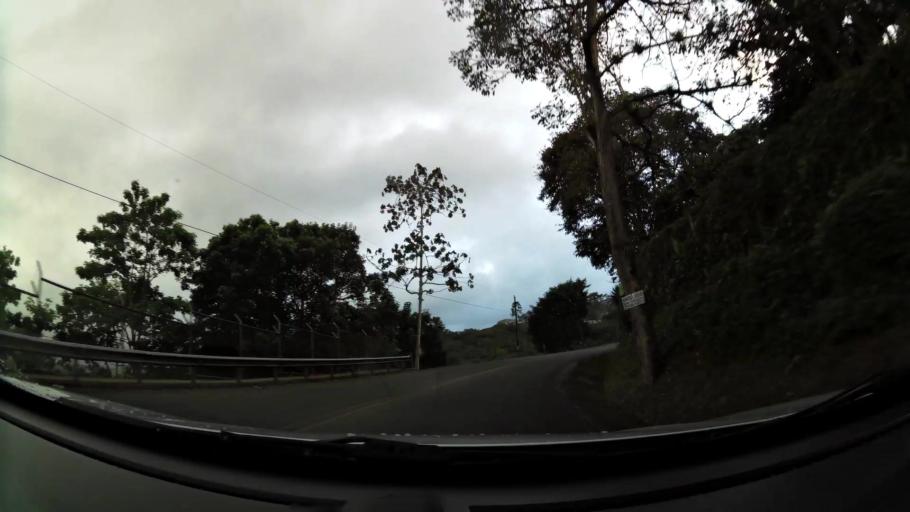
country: CR
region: Cartago
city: Turrialba
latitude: 9.9024
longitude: -83.6867
